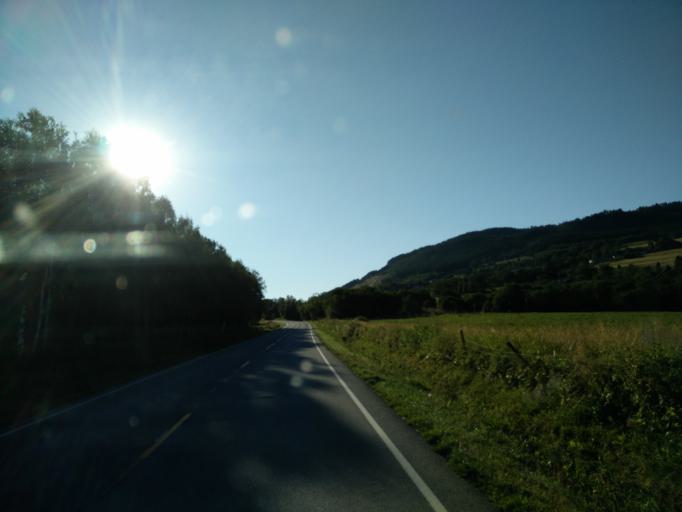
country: NO
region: More og Romsdal
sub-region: Halsa
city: Liaboen
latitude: 63.0723
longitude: 8.2718
